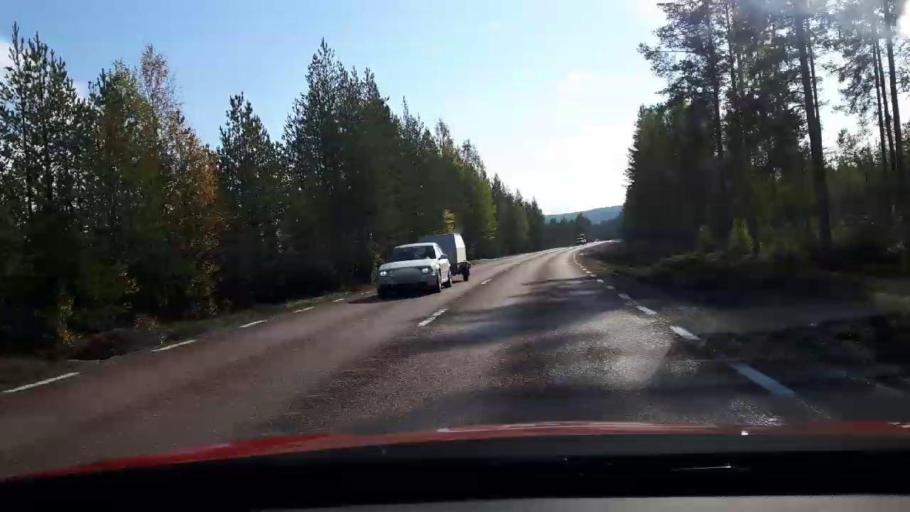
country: SE
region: Gaevleborg
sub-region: Ljusdals Kommun
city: Farila
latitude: 61.8989
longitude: 15.6495
